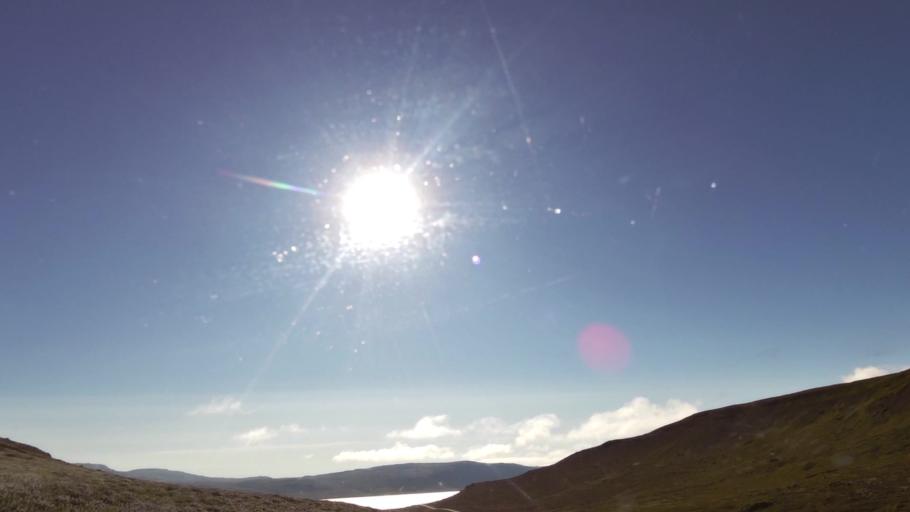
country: IS
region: West
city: Olafsvik
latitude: 65.5383
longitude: -23.8294
